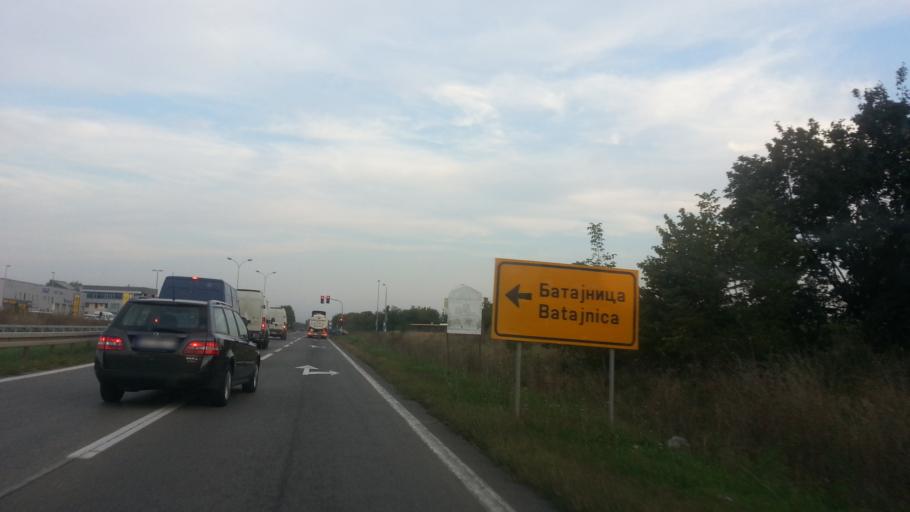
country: RS
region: Central Serbia
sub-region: Belgrade
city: Zemun
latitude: 44.8730
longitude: 20.3327
